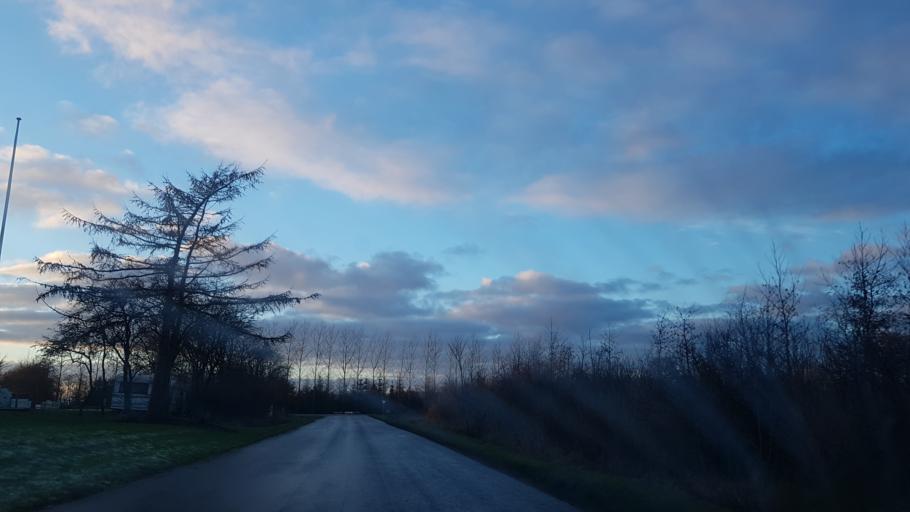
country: DK
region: South Denmark
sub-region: Kolding Kommune
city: Vamdrup
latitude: 55.3762
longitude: 9.2796
